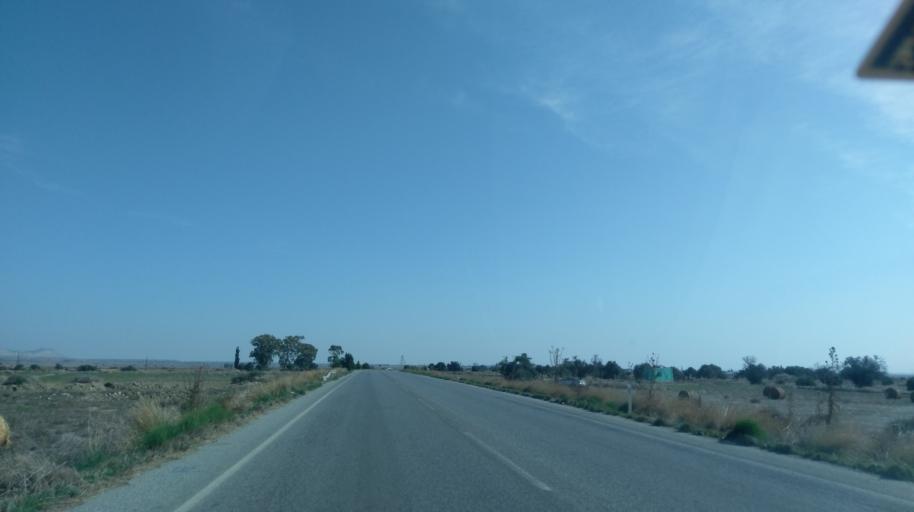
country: CY
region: Ammochostos
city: Lefkonoiko
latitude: 35.2600
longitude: 33.6645
